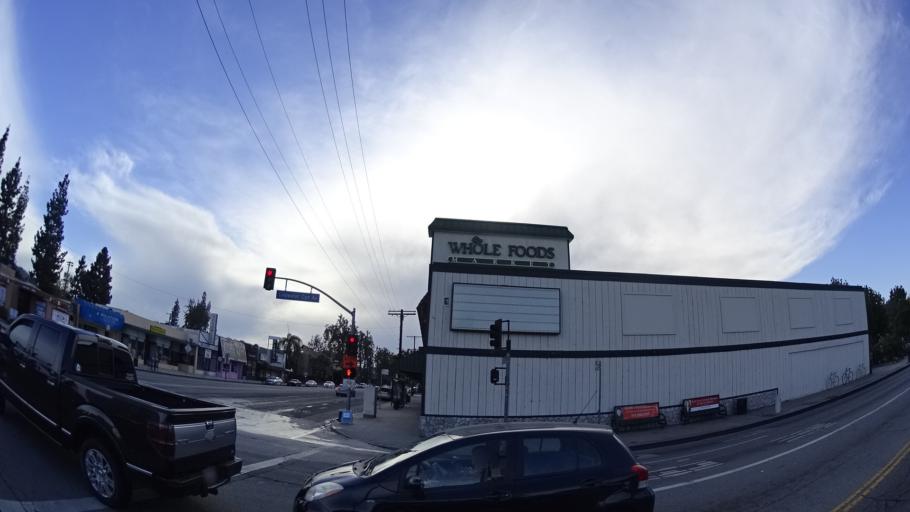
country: US
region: California
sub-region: Los Angeles County
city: Sherman Oaks
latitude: 34.1577
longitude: -118.4138
